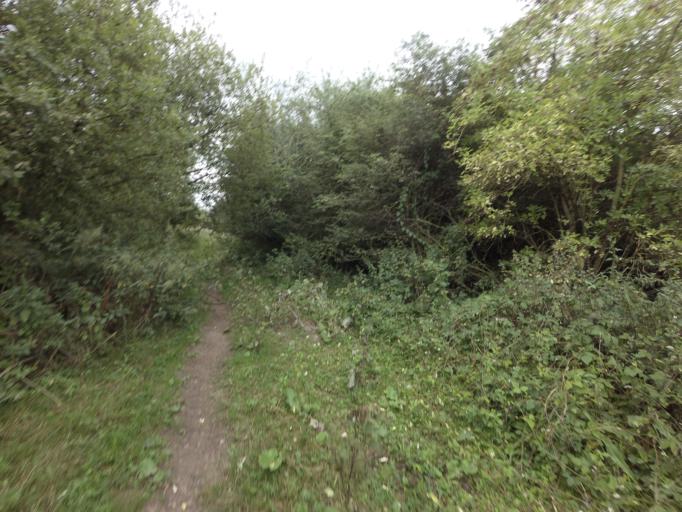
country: NL
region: Limburg
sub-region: Gemeente Maasgouw
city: Maasbracht
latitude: 51.1472
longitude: 5.8618
